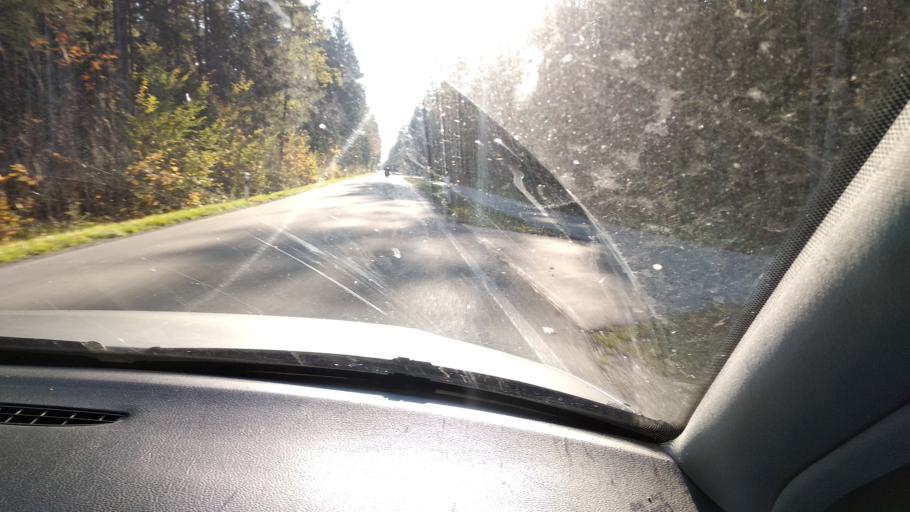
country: DE
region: Bavaria
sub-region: Upper Bavaria
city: Grasbrunn
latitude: 48.0440
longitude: 11.7562
